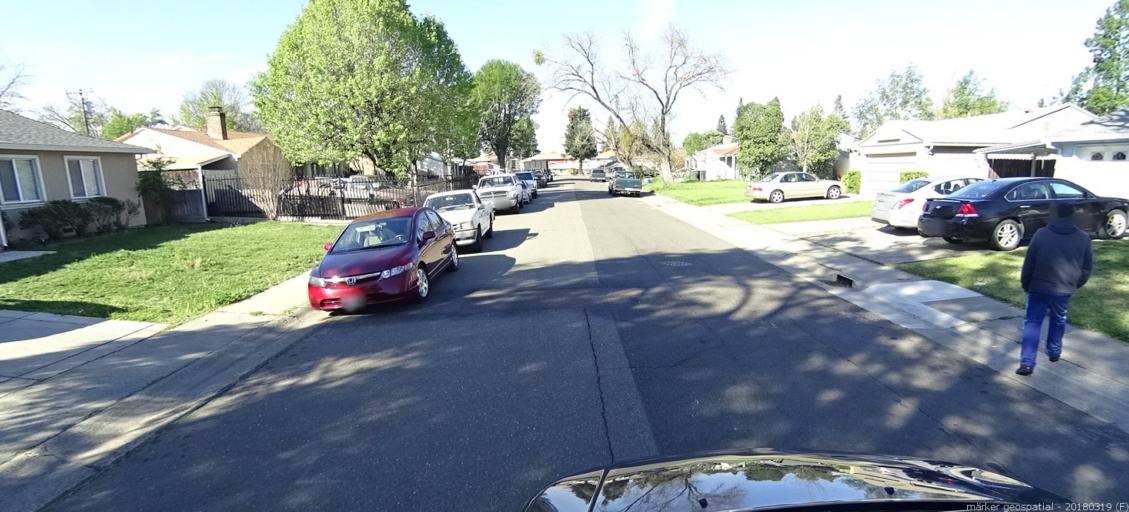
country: US
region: California
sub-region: Sacramento County
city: Parkway
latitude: 38.4886
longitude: -121.4538
